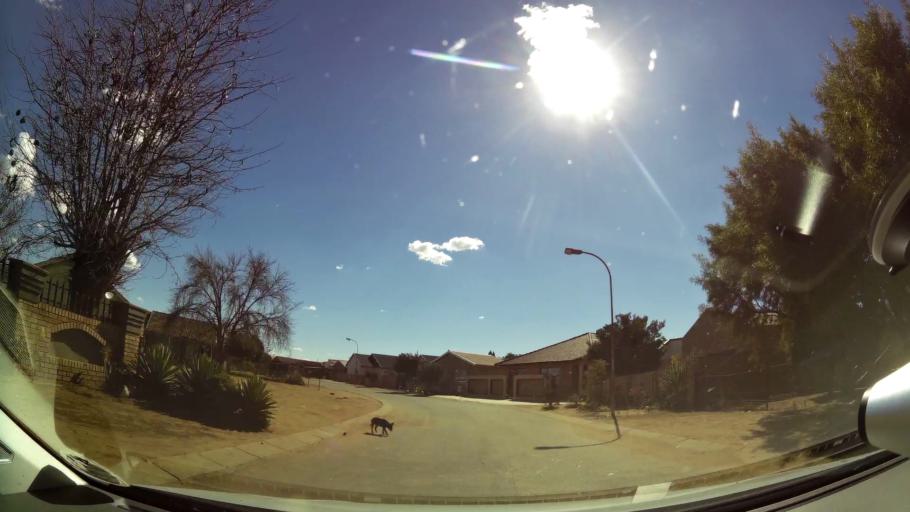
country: ZA
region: North-West
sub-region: Dr Kenneth Kaunda District Municipality
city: Klerksdorp
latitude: -26.8702
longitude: 26.5844
